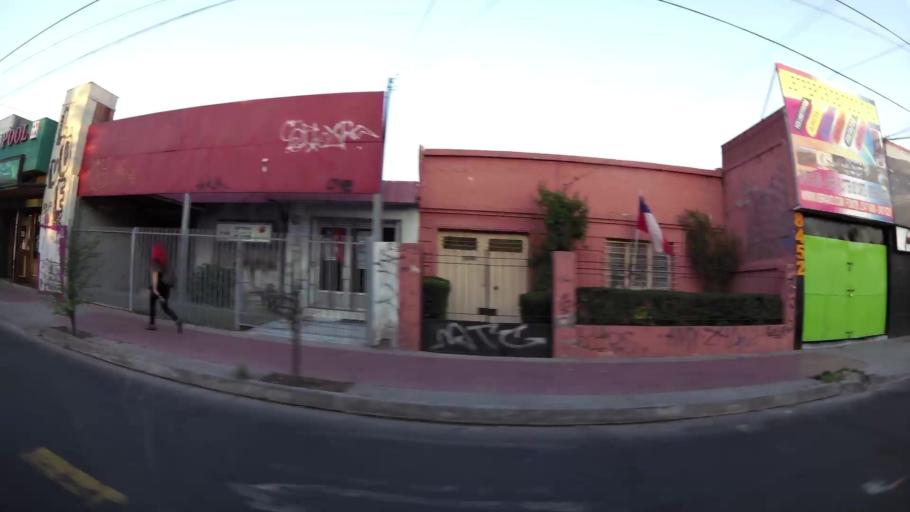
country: CL
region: Santiago Metropolitan
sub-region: Provincia de Santiago
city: La Pintana
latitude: -33.5325
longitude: -70.6629
